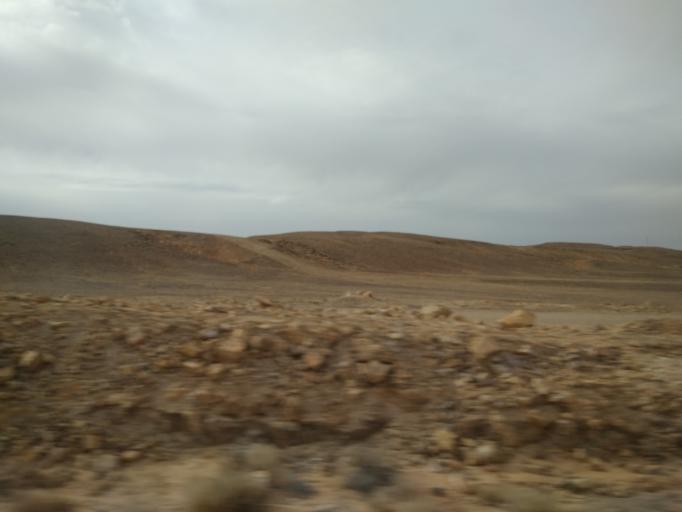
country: IL
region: Southern District
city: Eilat
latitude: 29.9137
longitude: 34.8784
